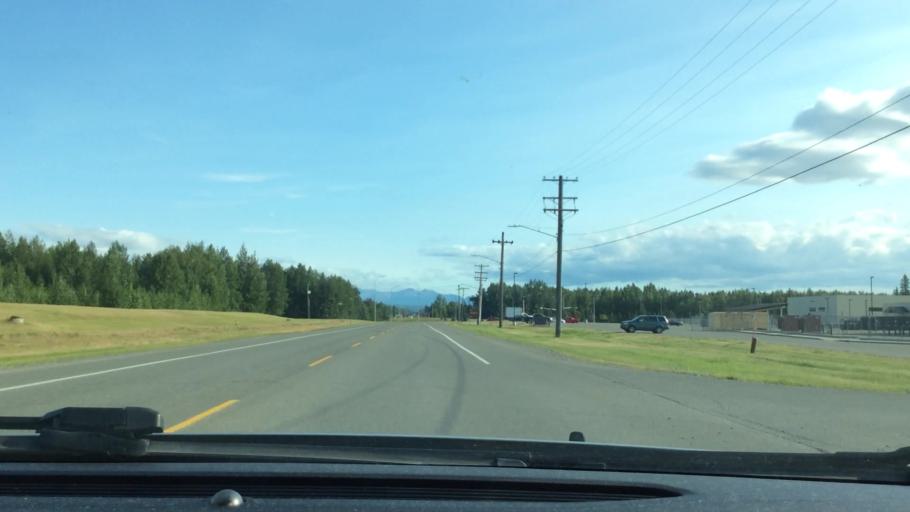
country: US
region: Alaska
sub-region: Anchorage Municipality
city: Anchorage
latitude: 61.2442
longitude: -149.7786
